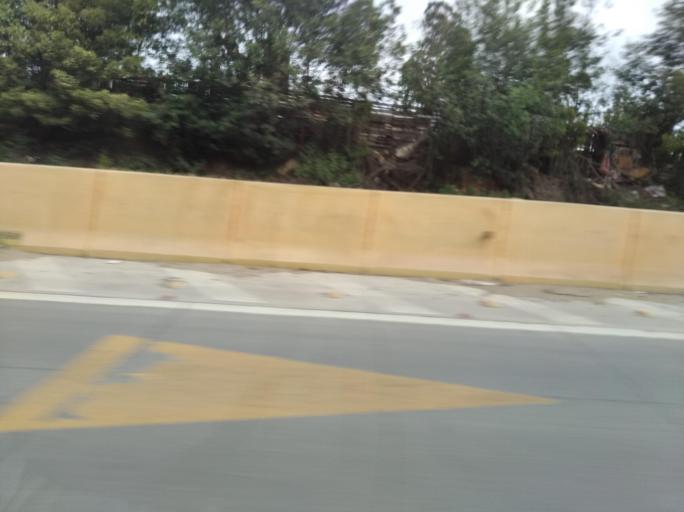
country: CL
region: Valparaiso
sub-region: Provincia de Valparaiso
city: Vina del Mar
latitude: -33.1072
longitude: -71.5685
